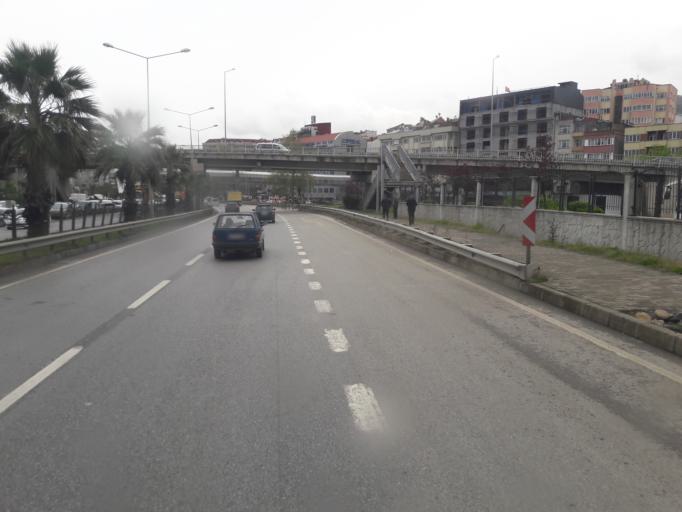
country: TR
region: Trabzon
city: Trabzon
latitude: 41.0095
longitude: 39.7261
